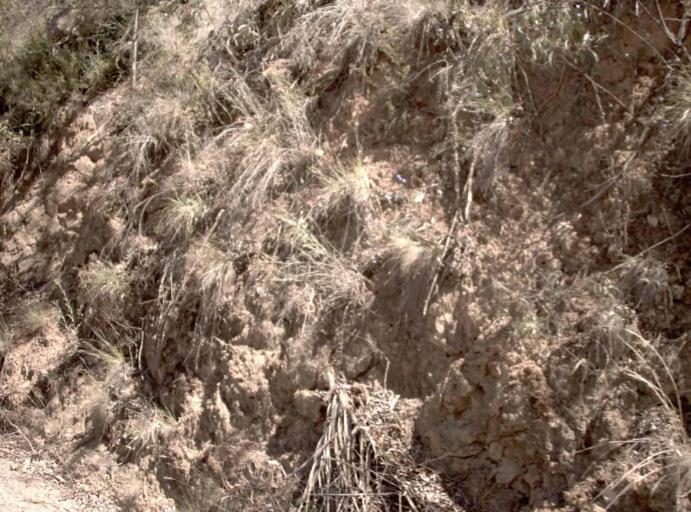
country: AU
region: New South Wales
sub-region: Snowy River
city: Jindabyne
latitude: -37.0396
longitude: 148.5550
